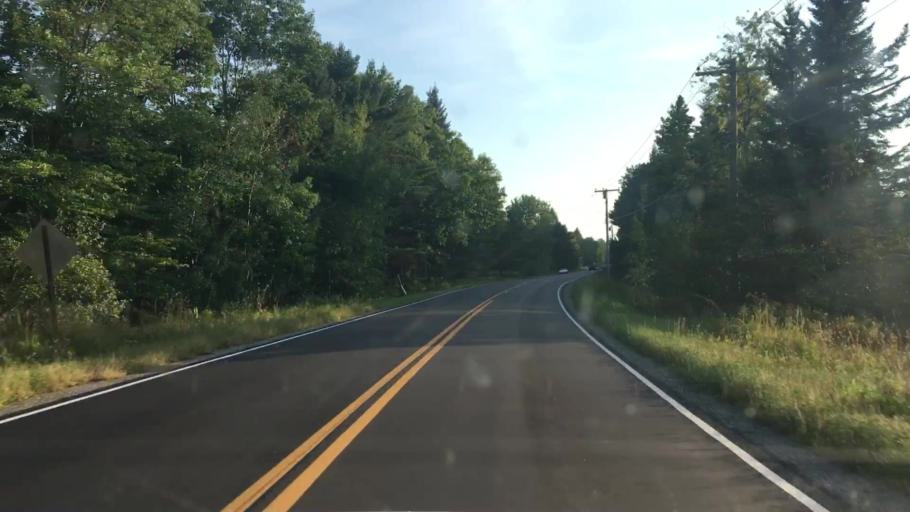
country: US
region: Maine
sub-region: Penobscot County
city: Hampden
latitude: 44.7254
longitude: -68.8787
